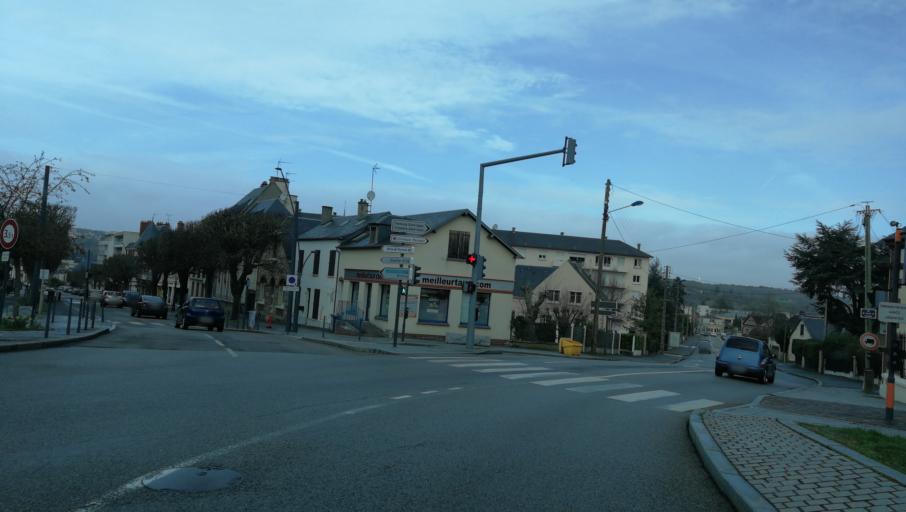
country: FR
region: Haute-Normandie
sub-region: Departement de l'Eure
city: Evreux
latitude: 49.0207
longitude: 1.1566
